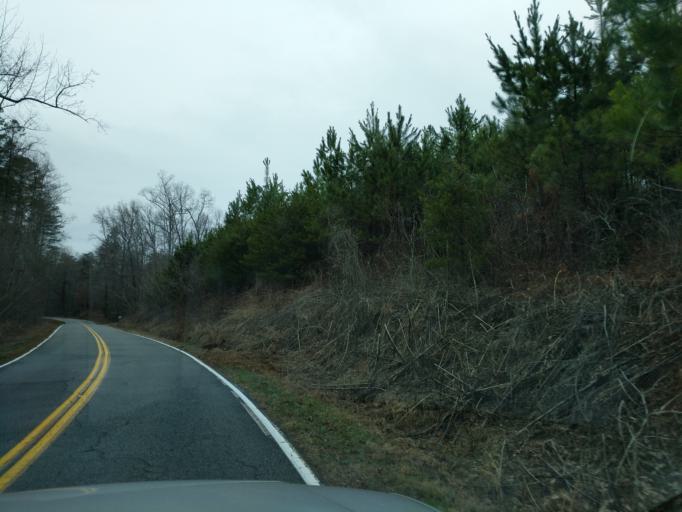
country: US
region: South Carolina
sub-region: Oconee County
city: Walhalla
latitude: 34.7949
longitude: -83.0911
